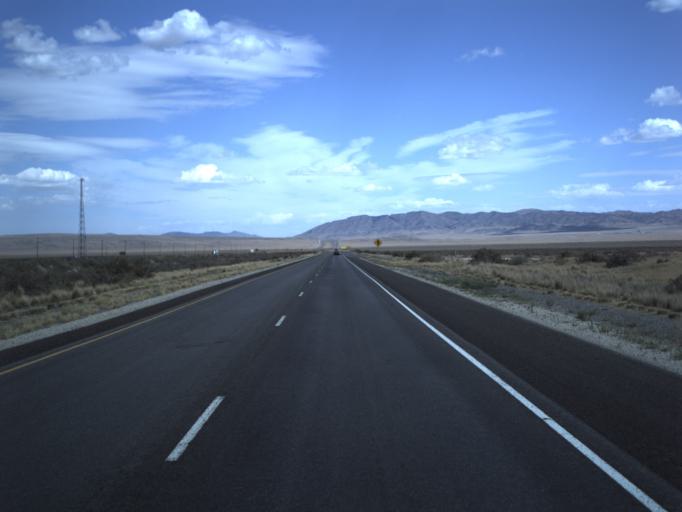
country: US
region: Utah
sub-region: Tooele County
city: Grantsville
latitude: 40.7319
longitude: -113.1121
